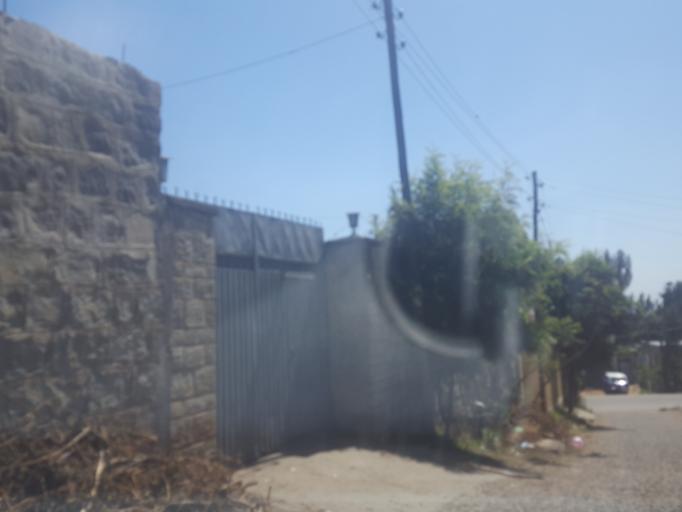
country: ET
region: Adis Abeba
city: Addis Ababa
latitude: 9.0623
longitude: 38.7416
